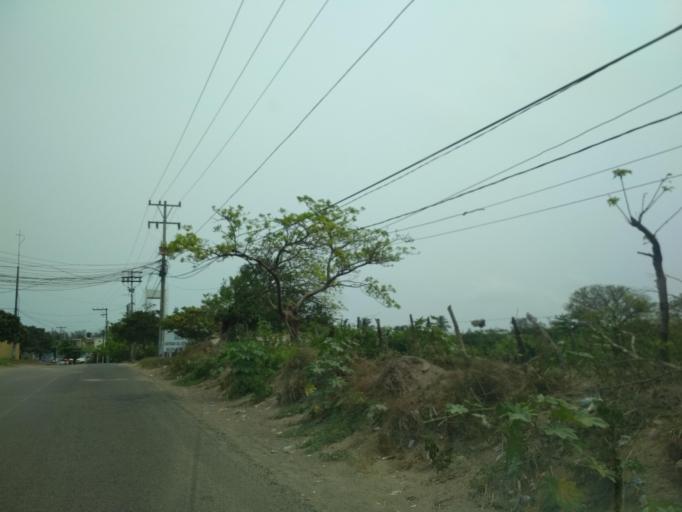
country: MX
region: Veracruz
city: Anton Lizardo
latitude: 19.0555
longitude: -95.9875
